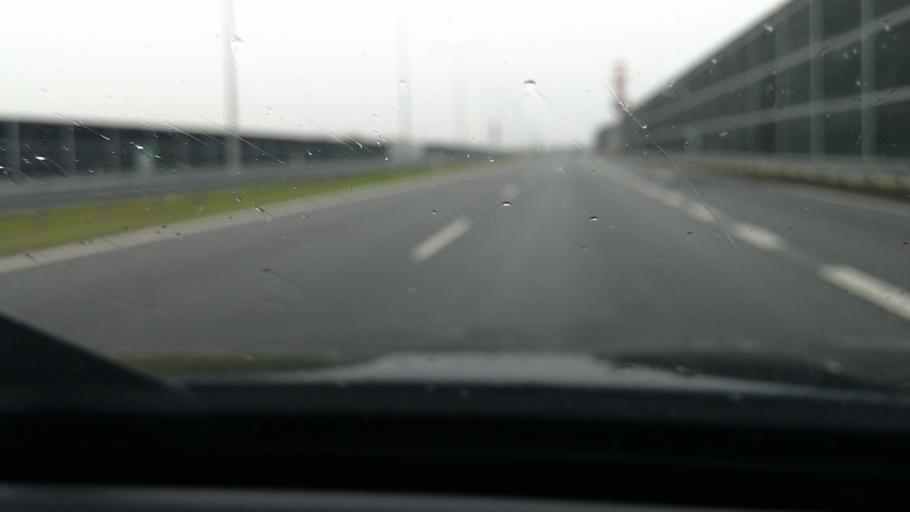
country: PL
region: Masovian Voivodeship
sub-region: Powiat zyrardowski
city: Zyrardow
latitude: 52.1127
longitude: 20.4710
